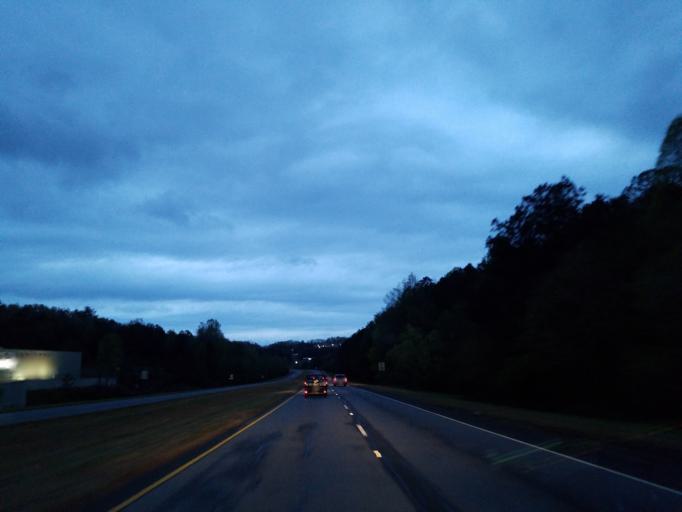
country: US
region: Georgia
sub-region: Gilmer County
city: Ellijay
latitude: 34.6762
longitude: -84.4799
